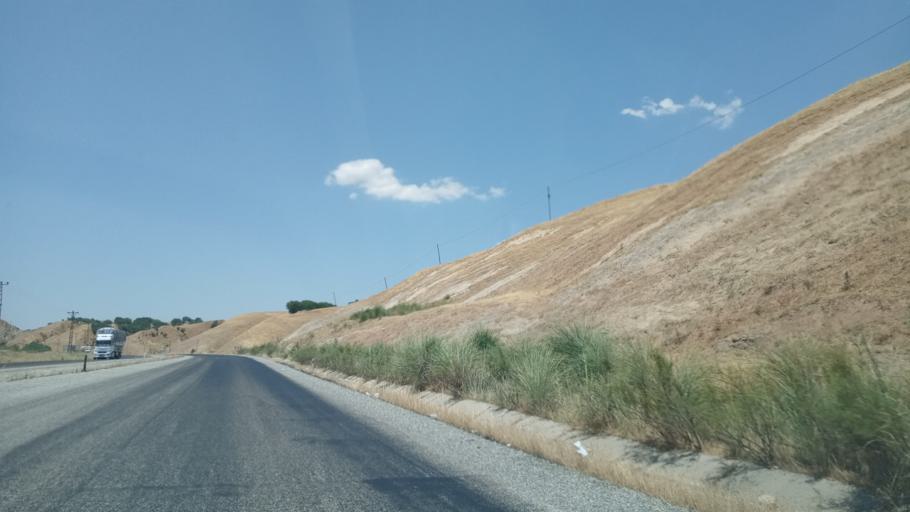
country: TR
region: Batman
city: Kozluk
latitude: 38.1687
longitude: 41.4664
